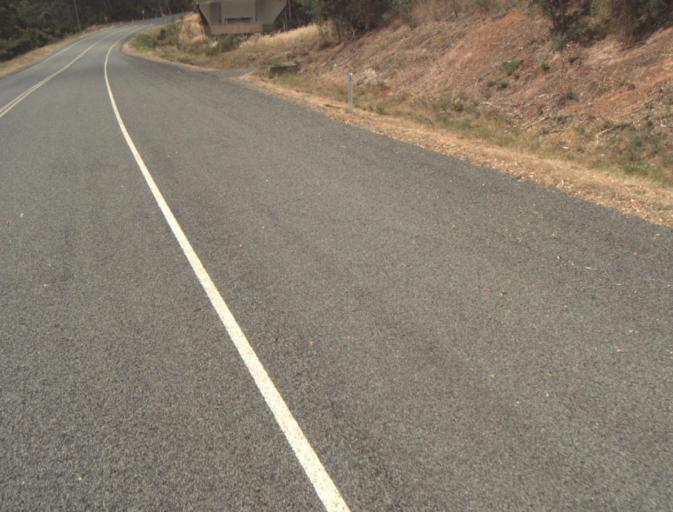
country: AU
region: Tasmania
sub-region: Launceston
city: Mayfield
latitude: -41.3052
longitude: 147.0487
